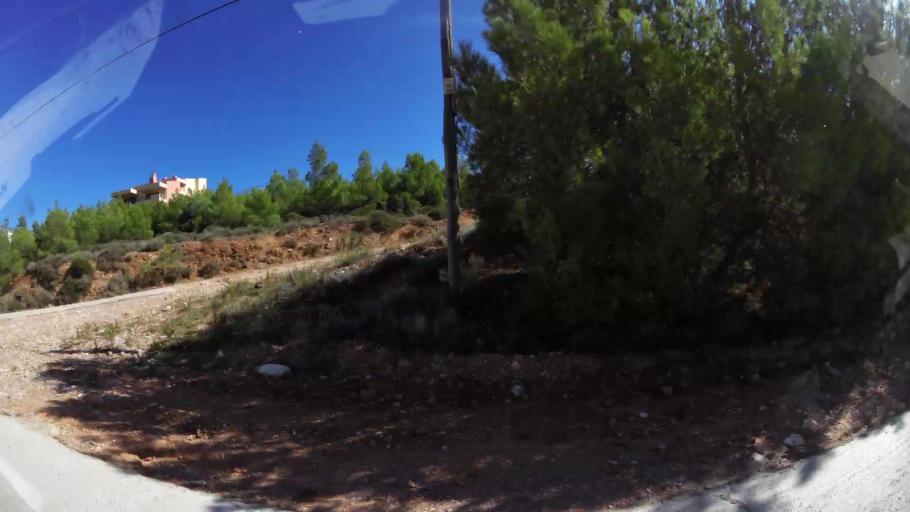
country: GR
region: Attica
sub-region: Nomarchia Anatolikis Attikis
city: Dioni
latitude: 38.0303
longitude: 23.9331
